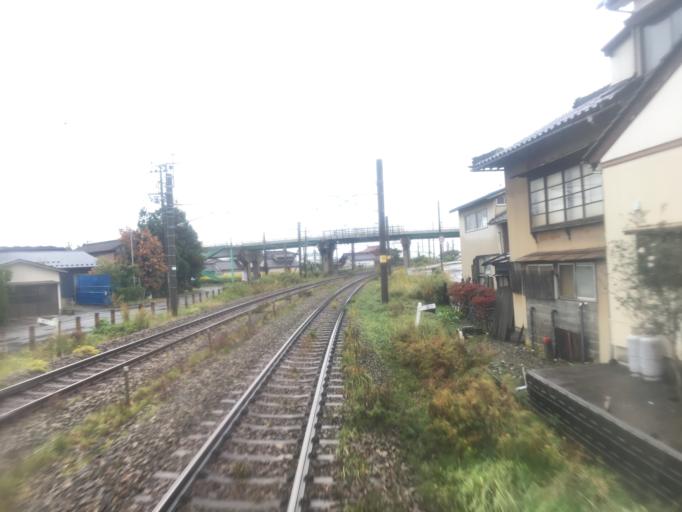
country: JP
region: Yamagata
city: Sakata
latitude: 38.8921
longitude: 139.9094
